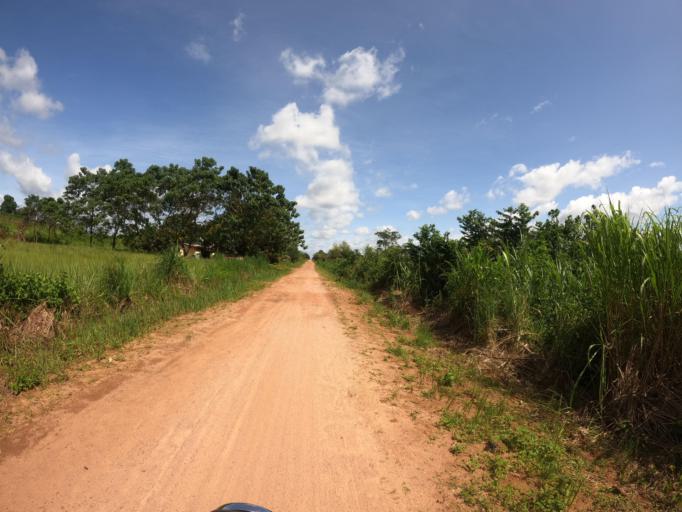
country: SL
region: Northern Province
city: Masingbi
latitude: 8.8327
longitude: -11.9942
